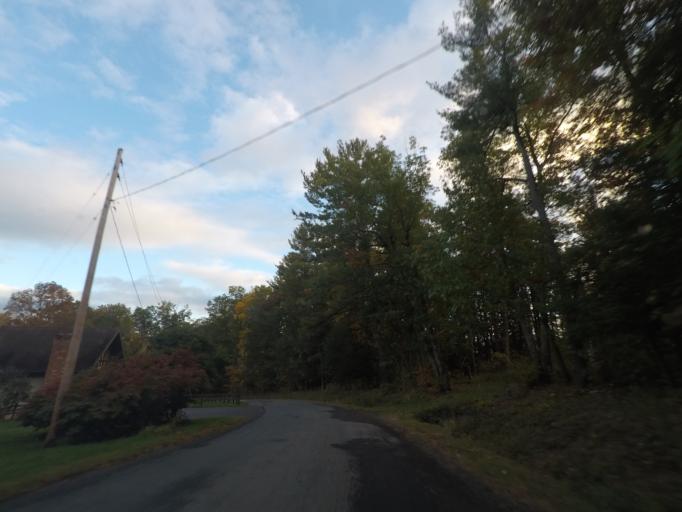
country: US
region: New York
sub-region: Rensselaer County
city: Nassau
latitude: 42.5409
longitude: -73.5792
